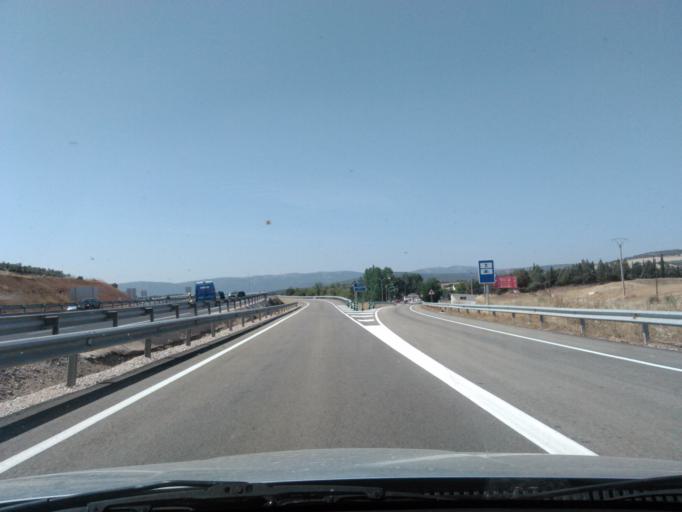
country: ES
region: Castille-La Mancha
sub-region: Provincia de Ciudad Real
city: Viso del Marques
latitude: 38.5000
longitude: -3.5024
